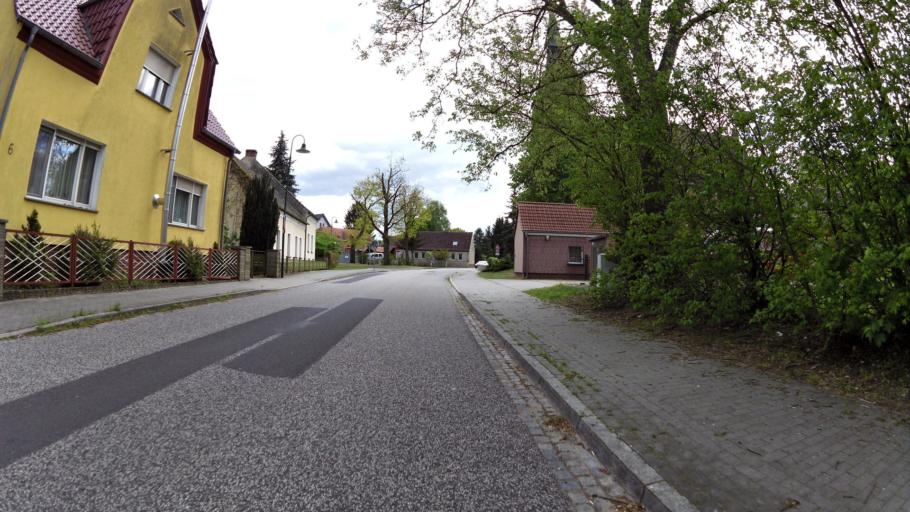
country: DE
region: Brandenburg
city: Rauen
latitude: 52.3275
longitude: 13.9497
